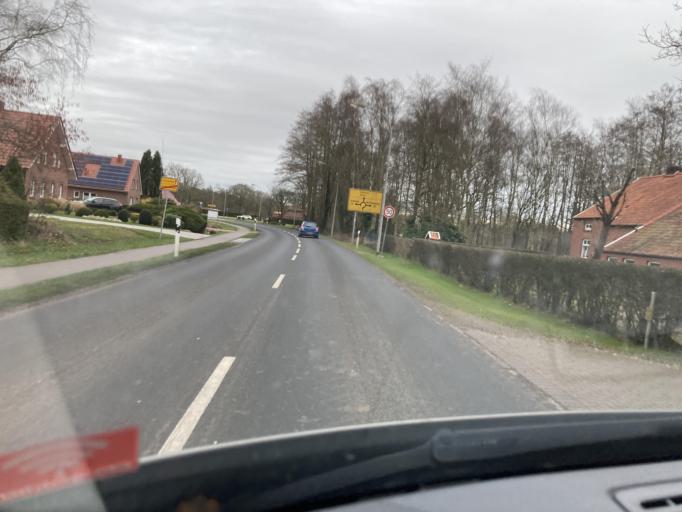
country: DE
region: Lower Saxony
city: Papenburg
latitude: 53.1314
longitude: 7.4739
